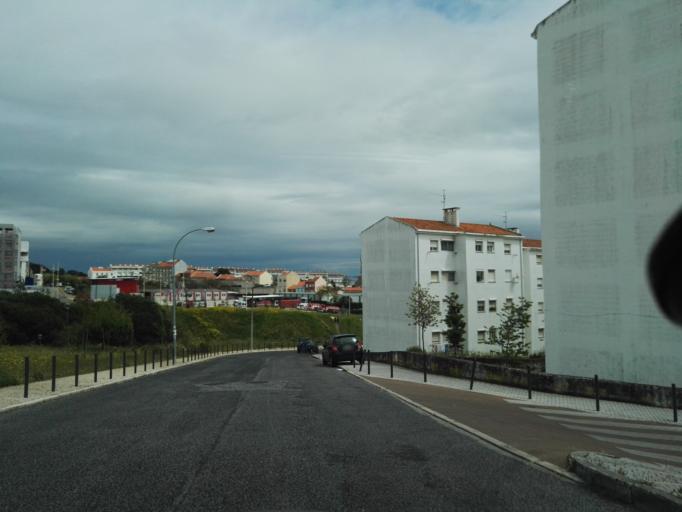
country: PT
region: Lisbon
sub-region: Oeiras
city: Alges
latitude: 38.7114
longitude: -9.1973
